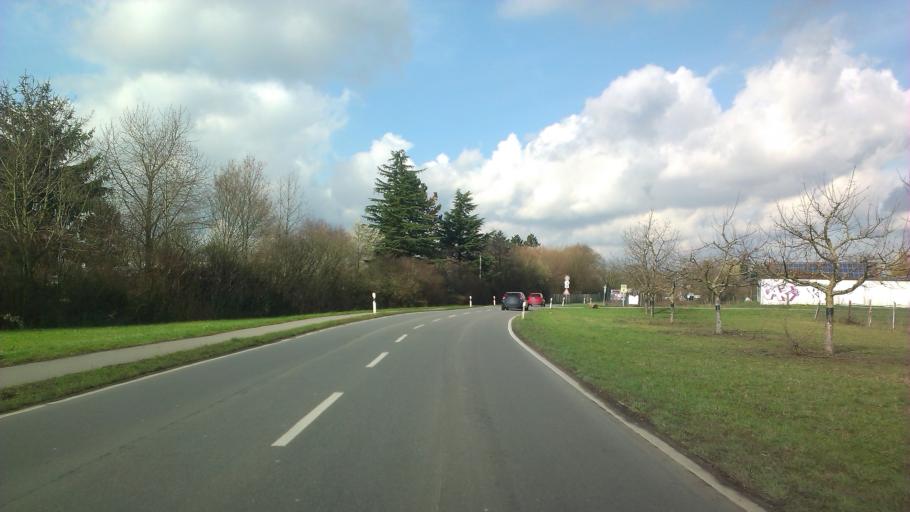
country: DE
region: Baden-Wuerttemberg
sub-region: Karlsruhe Region
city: Eppelheim
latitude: 49.3973
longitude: 8.6553
